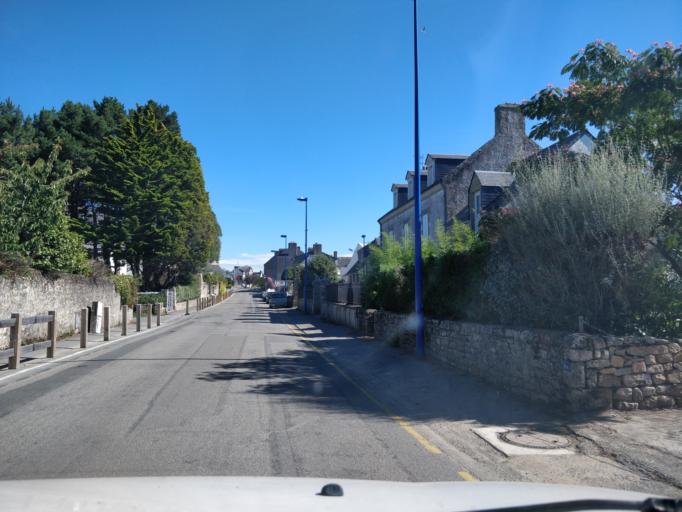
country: FR
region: Brittany
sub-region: Departement du Morbihan
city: Locmariaquer
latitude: 47.5709
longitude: -2.9472
